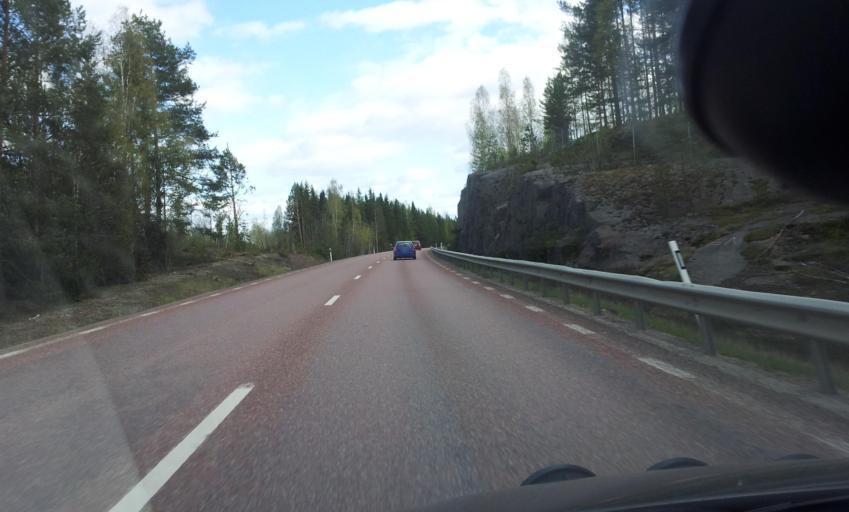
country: SE
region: Gaevleborg
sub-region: Ljusdals Kommun
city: Jaervsoe
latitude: 61.7739
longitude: 16.1512
